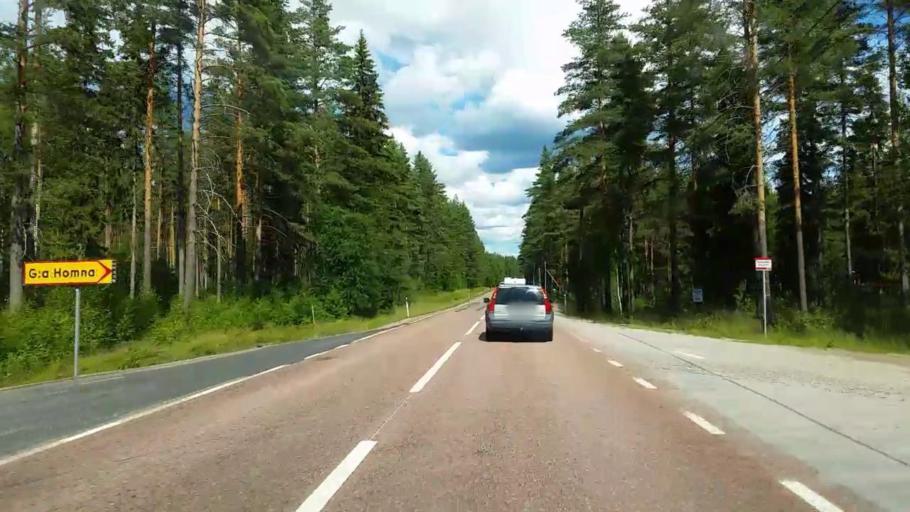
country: SE
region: Gaevleborg
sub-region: Ovanakers Kommun
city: Edsbyn
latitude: 61.3473
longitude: 15.6739
